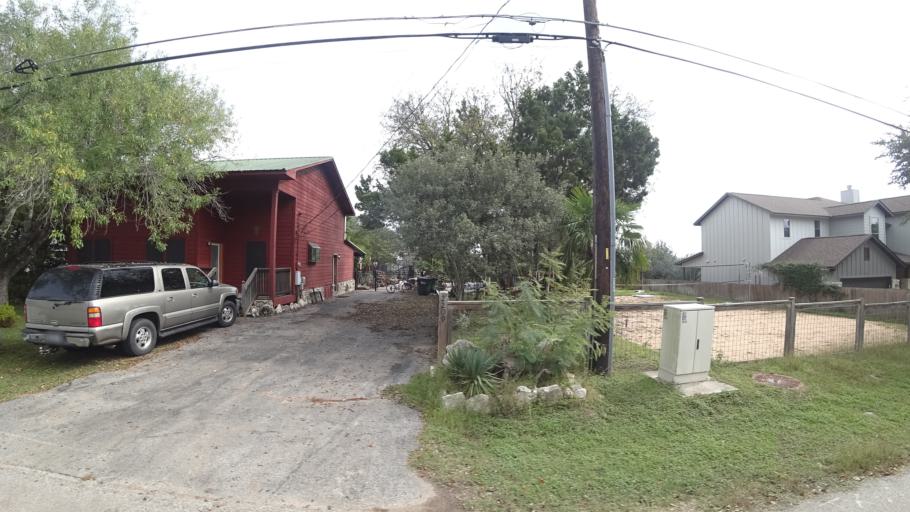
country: US
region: Texas
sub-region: Travis County
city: Hudson Bend
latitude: 30.3741
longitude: -97.9200
